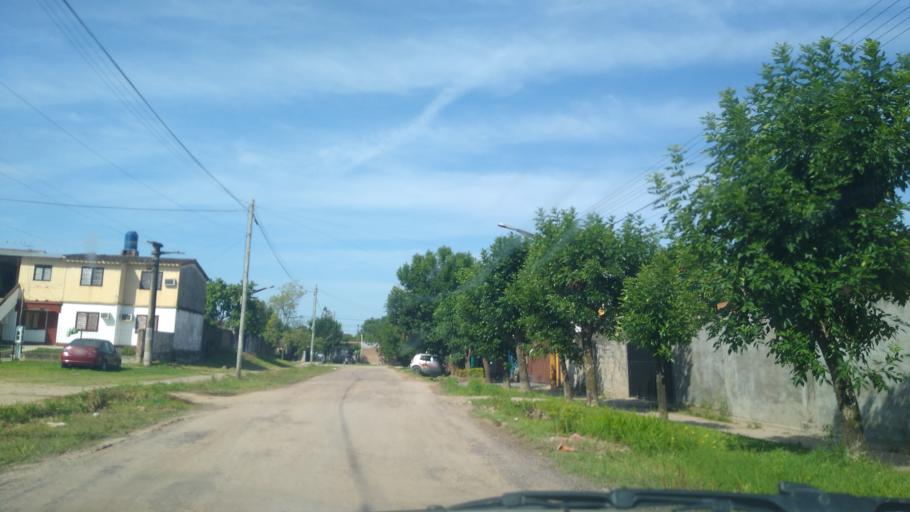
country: AR
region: Chaco
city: Puerto Vilelas
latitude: -27.4988
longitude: -58.9574
